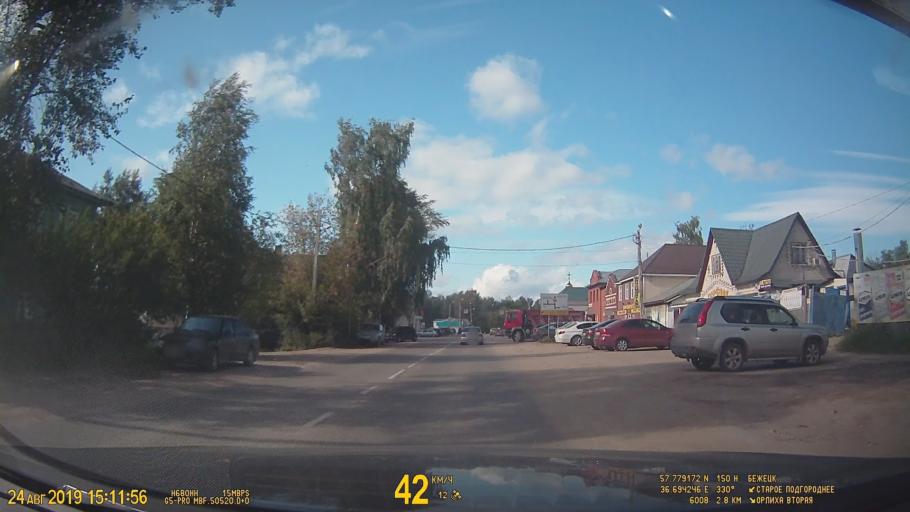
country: RU
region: Tverskaya
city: Bezhetsk
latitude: 57.7794
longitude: 36.6940
